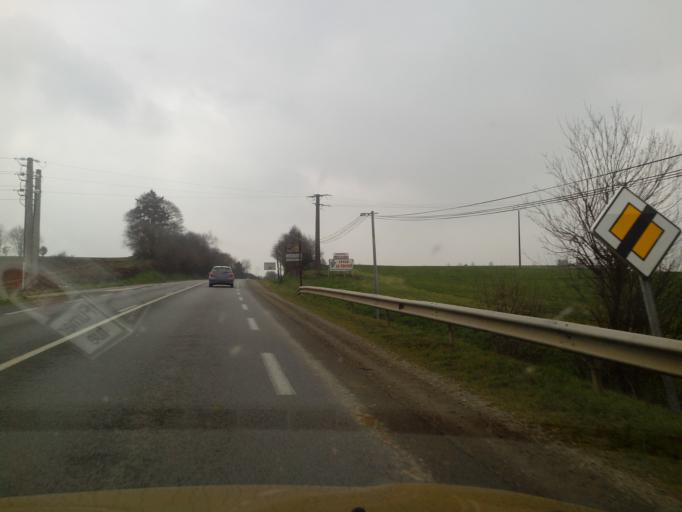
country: FR
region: Brittany
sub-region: Departement du Morbihan
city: Ploermel
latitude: 47.9493
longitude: -2.3957
